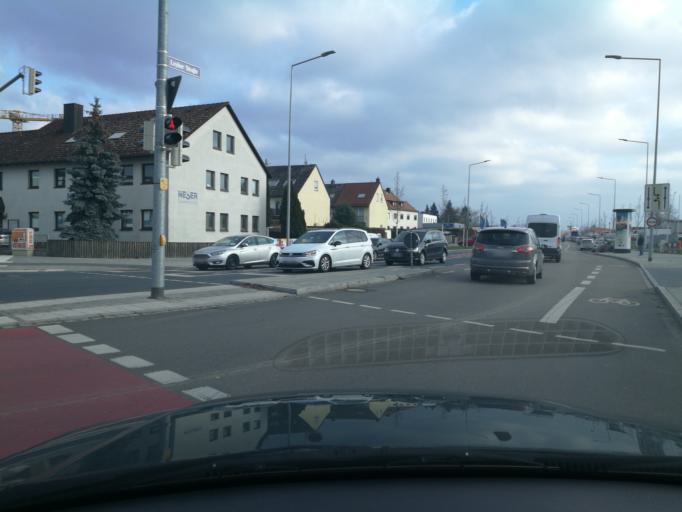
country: DE
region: Bavaria
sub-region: Regierungsbezirk Mittelfranken
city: Grossreuth bei Schweinau
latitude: 49.4541
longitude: 11.0090
